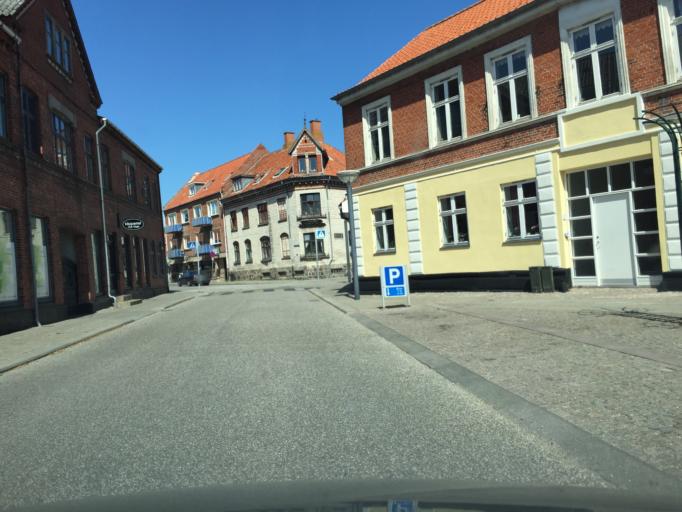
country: DK
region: Zealand
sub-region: Vordingborg Kommune
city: Stege
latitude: 54.9862
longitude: 12.2886
